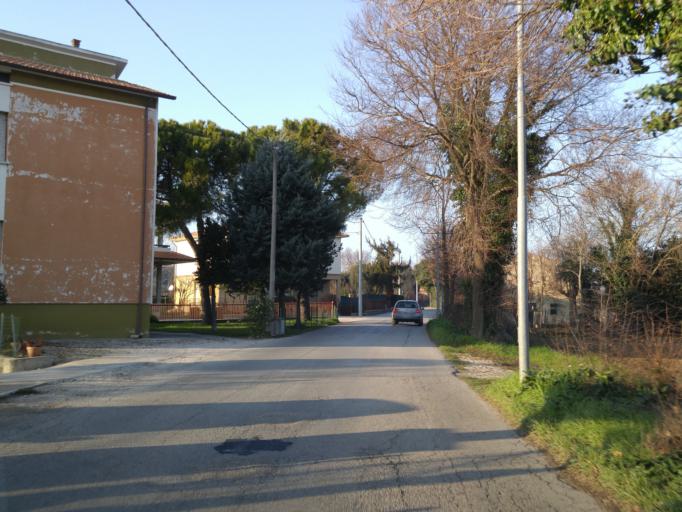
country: IT
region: The Marches
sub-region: Provincia di Pesaro e Urbino
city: Centinarola
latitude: 43.8240
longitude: 12.9950
